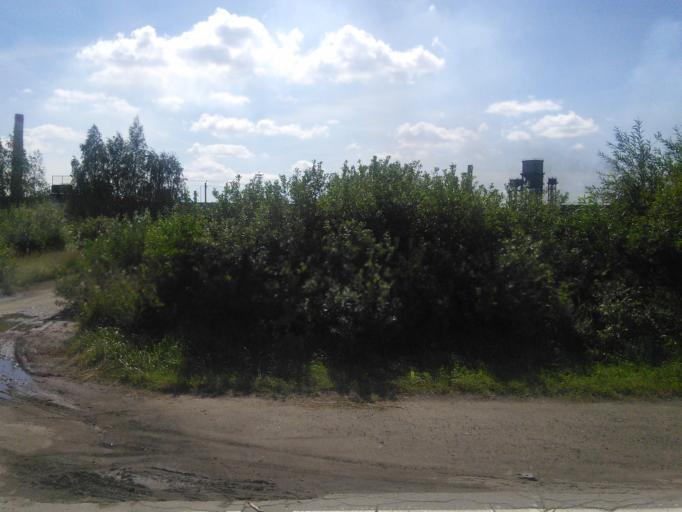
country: RU
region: Vologda
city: Cherepovets
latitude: 59.1535
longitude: 37.8806
